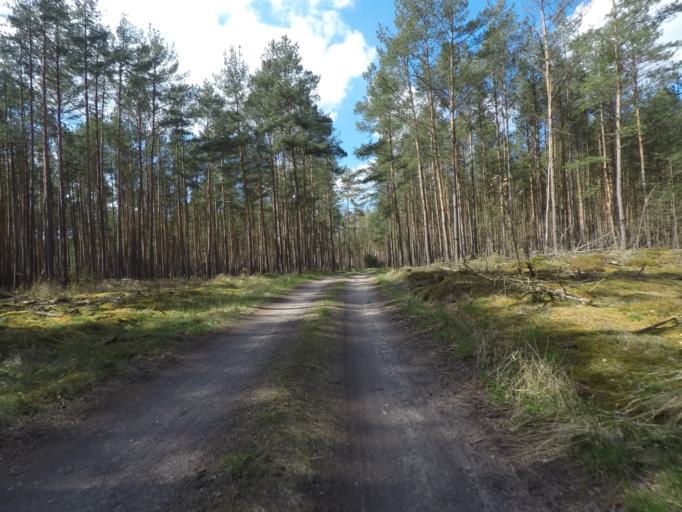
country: DE
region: Brandenburg
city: Melchow
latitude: 52.8194
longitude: 13.6891
